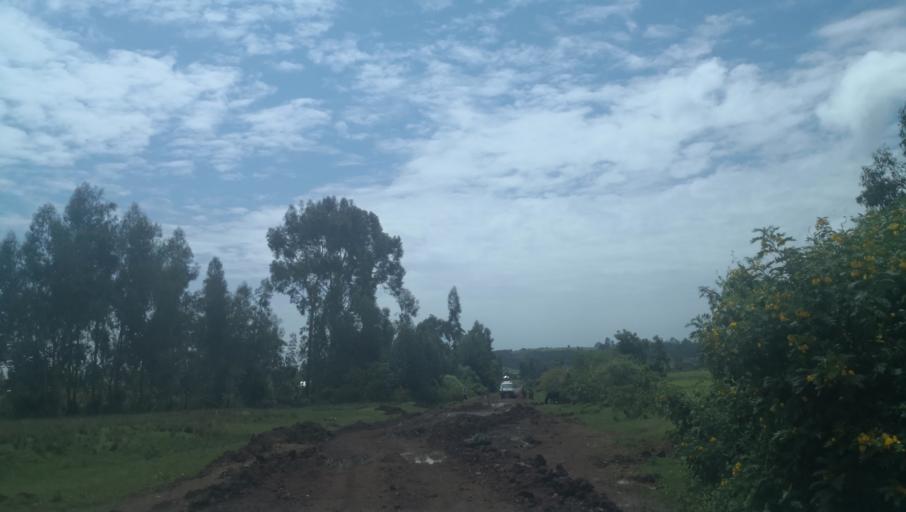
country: ET
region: Southern Nations, Nationalities, and People's Region
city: Butajira
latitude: 8.3047
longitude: 38.4642
